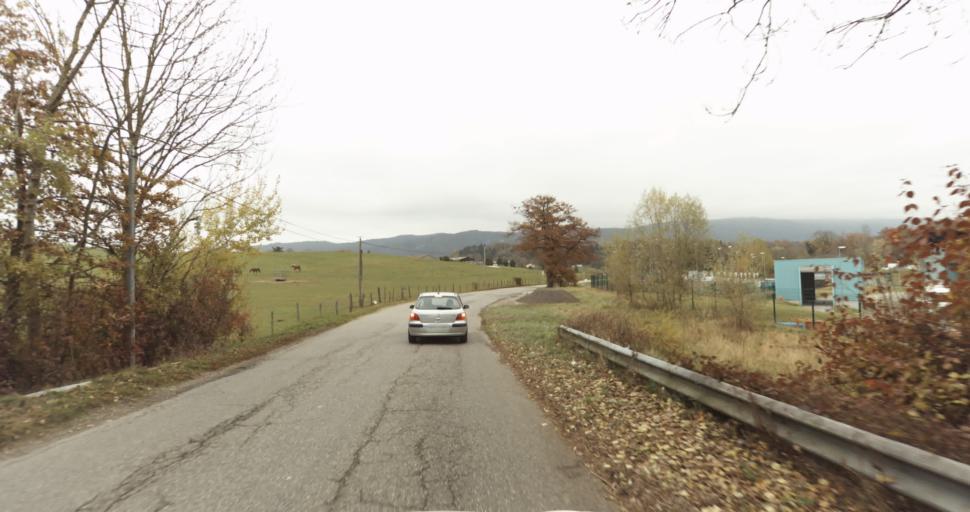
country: FR
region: Rhone-Alpes
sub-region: Departement de la Haute-Savoie
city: Seynod
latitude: 45.8732
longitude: 6.0691
